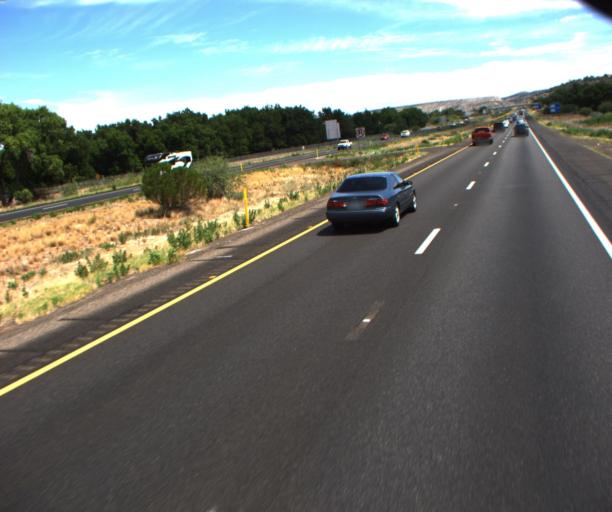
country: US
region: Arizona
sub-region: Yavapai County
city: Camp Verde
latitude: 34.5901
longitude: -111.8774
